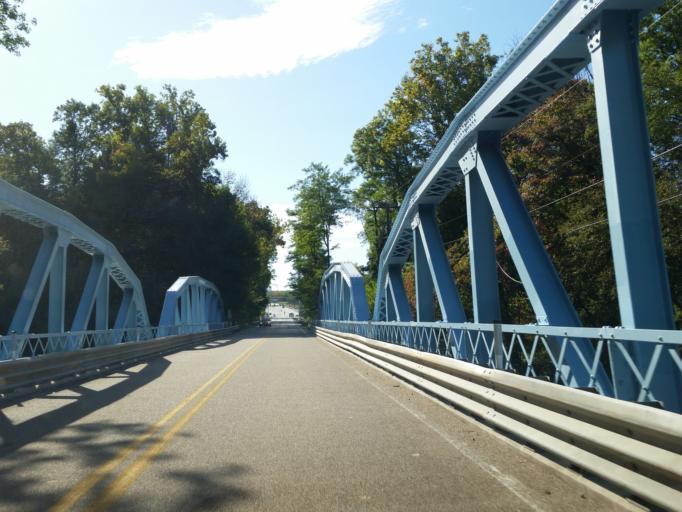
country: US
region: Pennsylvania
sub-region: Lebanon County
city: Jonestown
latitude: 40.4526
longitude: -76.5083
